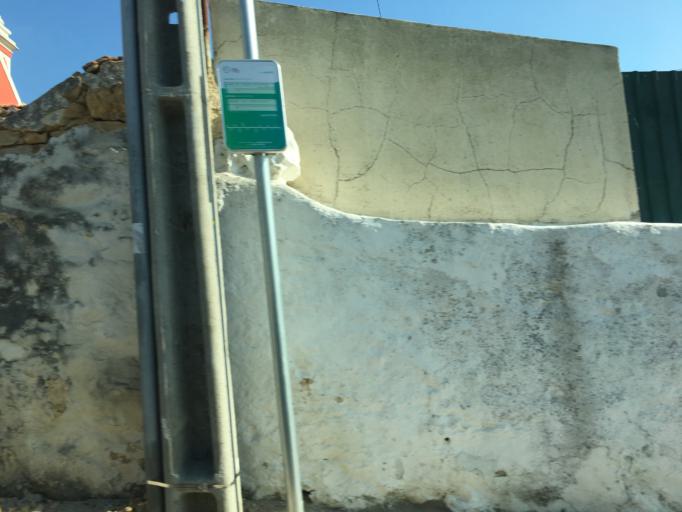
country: PT
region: Lisbon
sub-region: Cascais
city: Alcabideche
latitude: 38.7341
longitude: -9.3924
